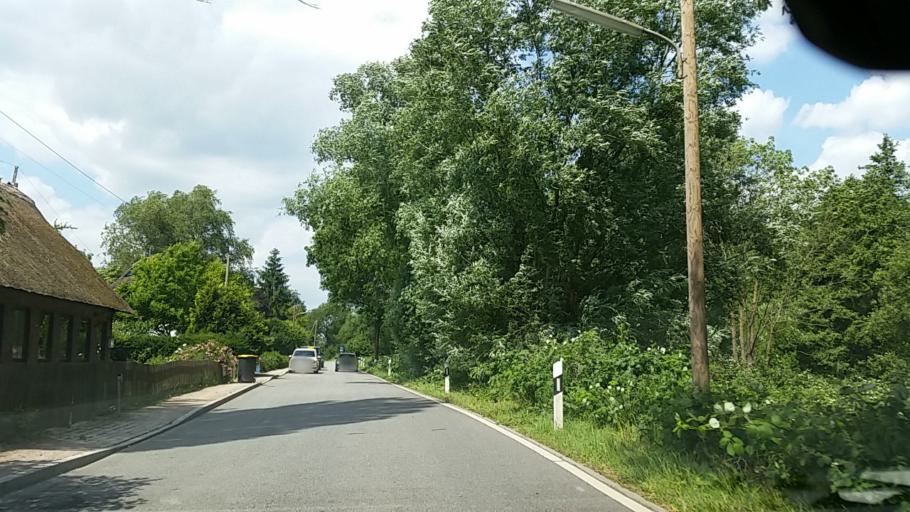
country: DE
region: Schleswig-Holstein
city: Oststeinbek
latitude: 53.5067
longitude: 10.1326
